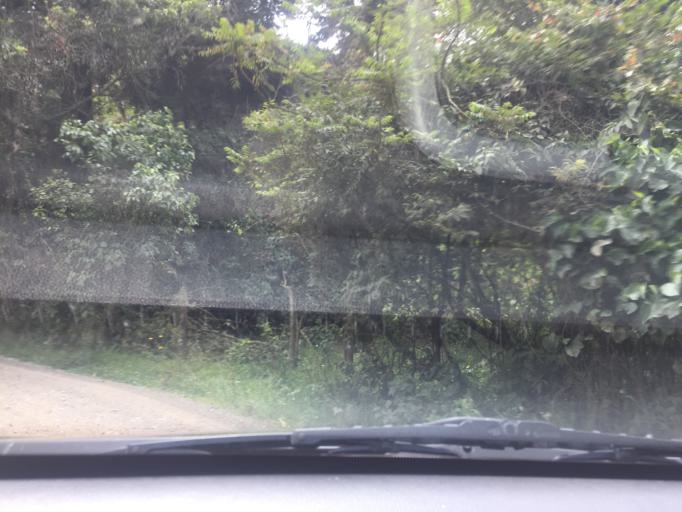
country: CO
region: Cundinamarca
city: Zipacon
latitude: 4.7871
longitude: -74.3757
